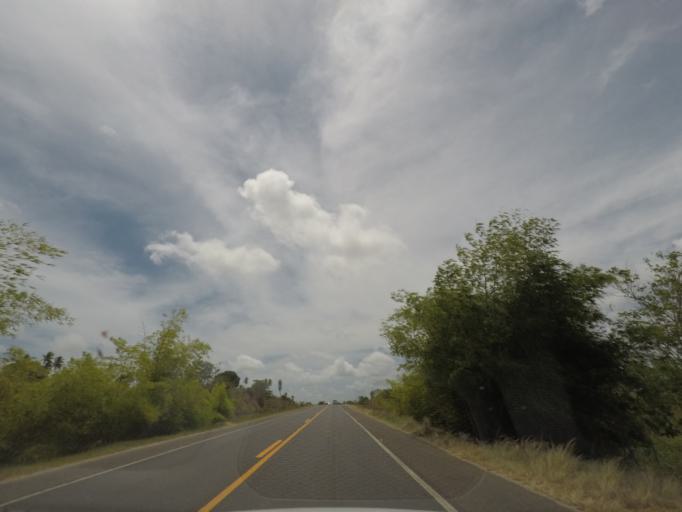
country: BR
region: Bahia
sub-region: Conde
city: Conde
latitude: -11.8098
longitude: -37.6324
